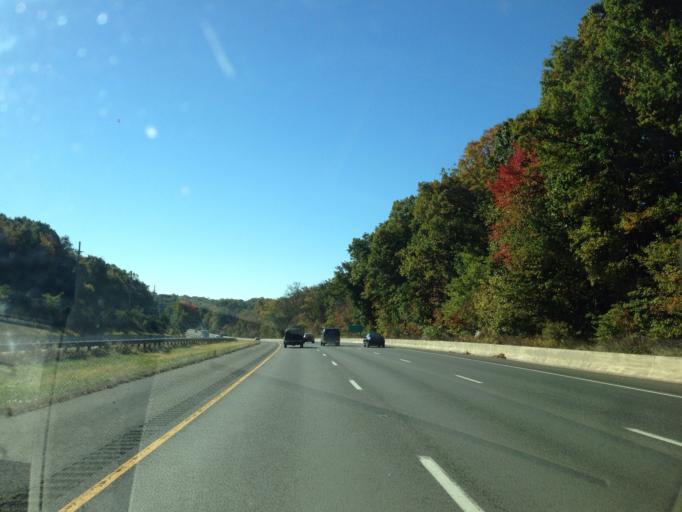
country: US
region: Maryland
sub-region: Montgomery County
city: Clarksburg
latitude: 39.2127
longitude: -77.2768
